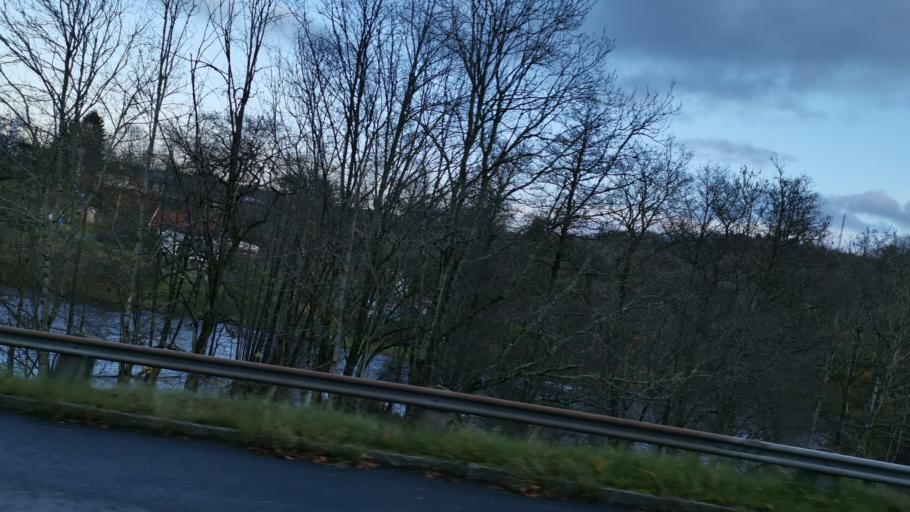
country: SE
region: Vaestra Goetaland
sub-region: Munkedals Kommun
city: Munkedal
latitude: 58.4742
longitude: 11.6748
